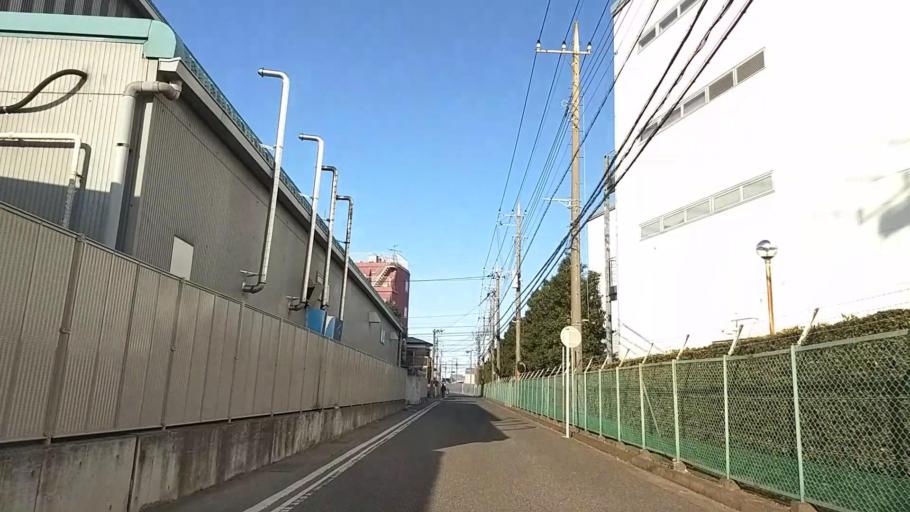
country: JP
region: Kanagawa
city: Atsugi
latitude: 35.4471
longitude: 139.3394
